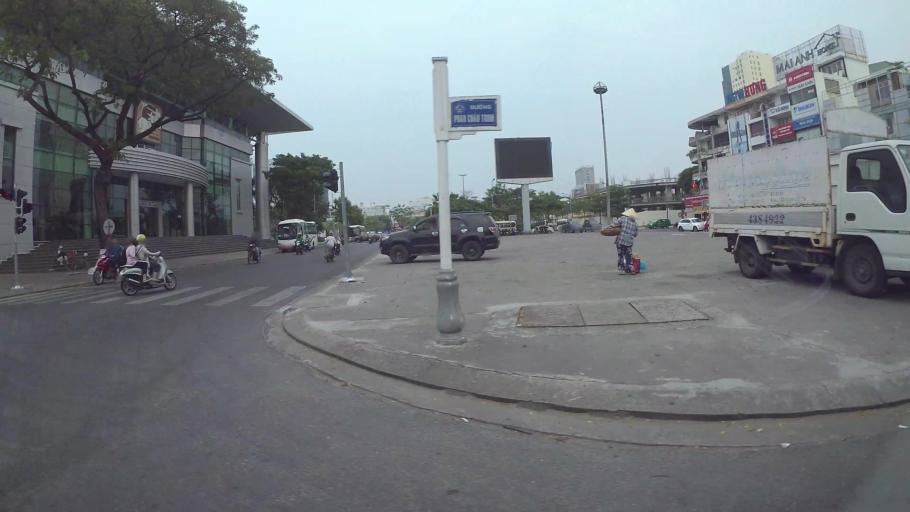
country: VN
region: Da Nang
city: Da Nang
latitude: 16.0685
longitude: 108.2204
